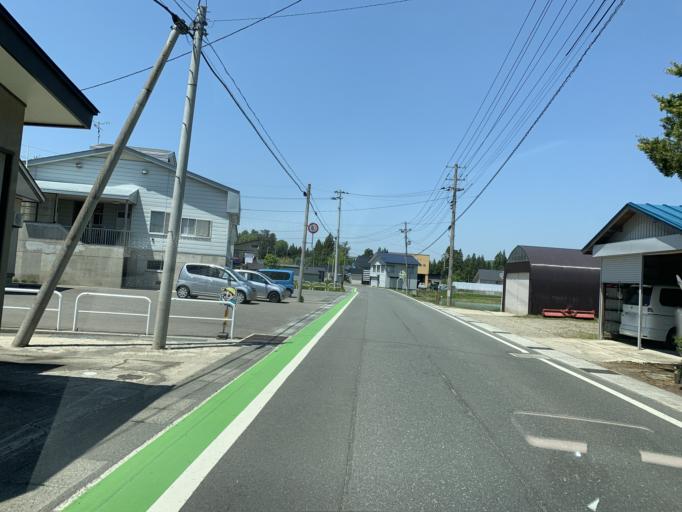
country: JP
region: Akita
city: Yokotemachi
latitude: 39.3515
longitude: 140.7695
